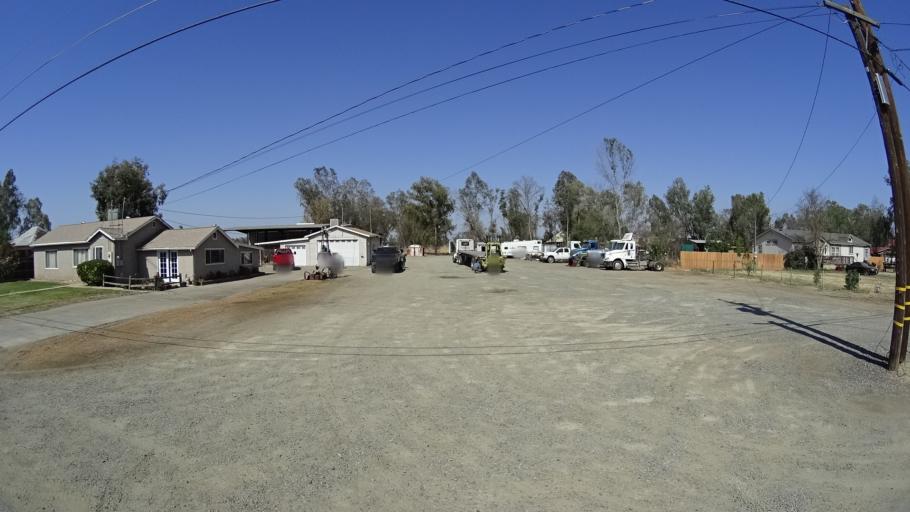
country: US
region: California
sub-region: Kings County
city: Home Garden
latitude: 36.3110
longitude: -119.6302
